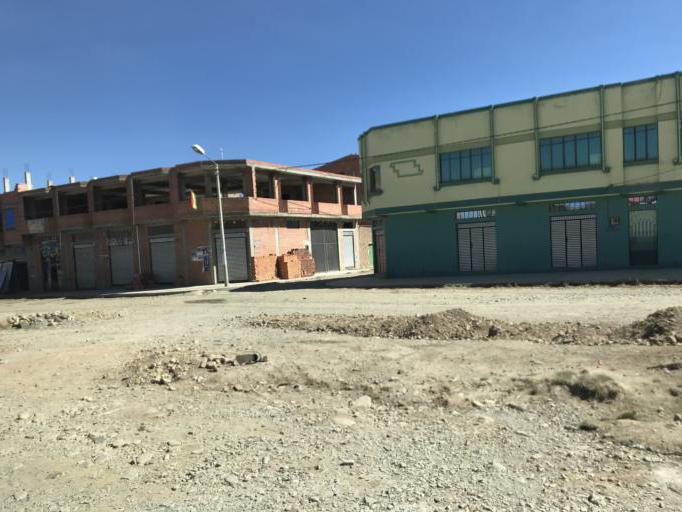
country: BO
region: La Paz
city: La Paz
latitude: -16.5022
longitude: -68.2431
